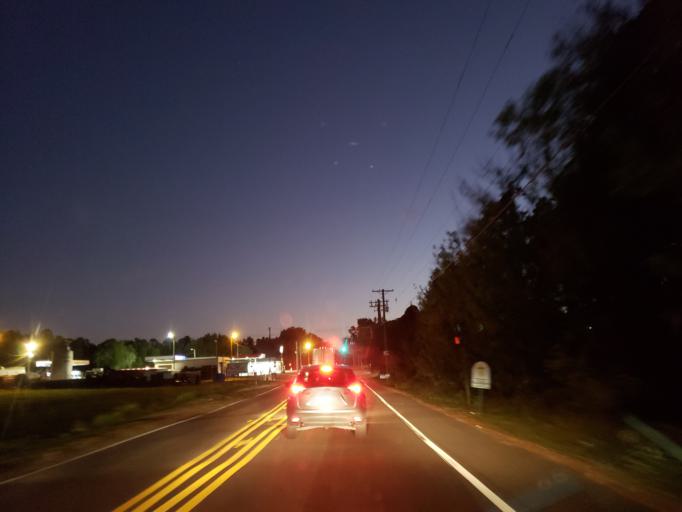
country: US
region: Florida
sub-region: Hillsborough County
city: Dover
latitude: 28.0223
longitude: -82.1871
